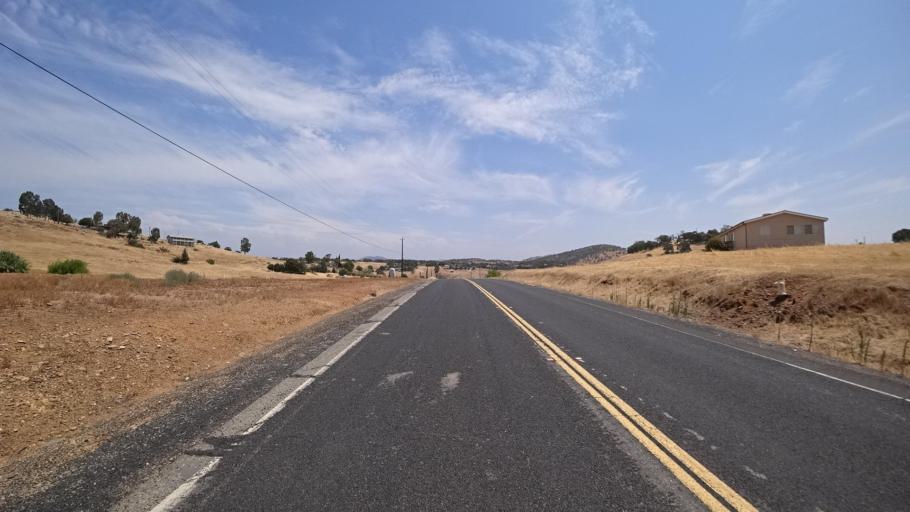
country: US
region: California
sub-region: Tuolumne County
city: Jamestown
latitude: 37.6409
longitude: -120.3380
